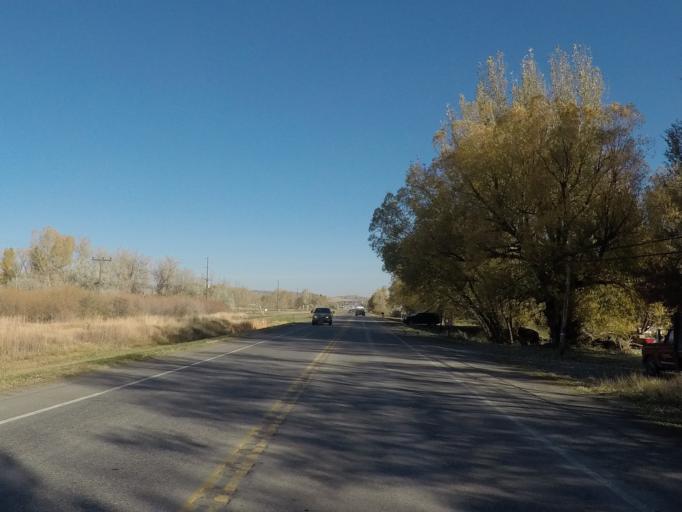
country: US
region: Montana
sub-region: Park County
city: Livingston
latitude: 45.6227
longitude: -110.5783
